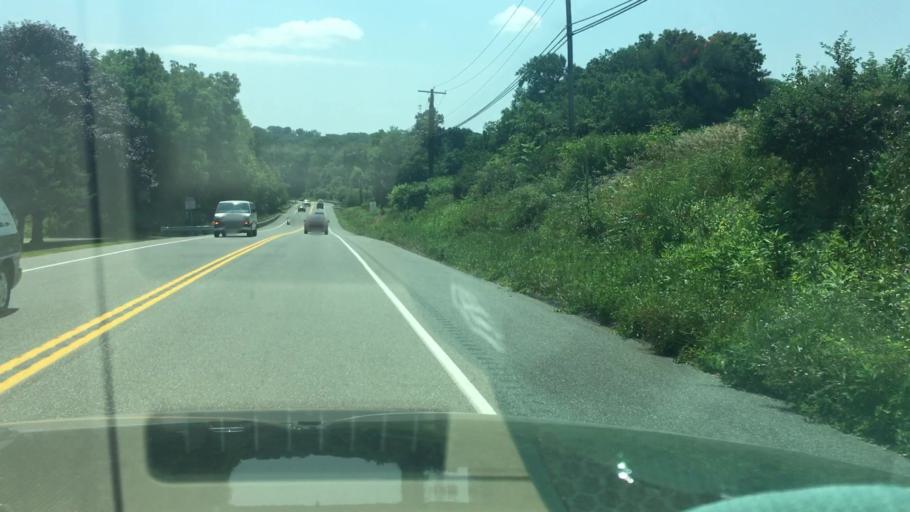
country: US
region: Pennsylvania
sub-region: Lehigh County
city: Schnecksville
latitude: 40.6788
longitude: -75.6938
